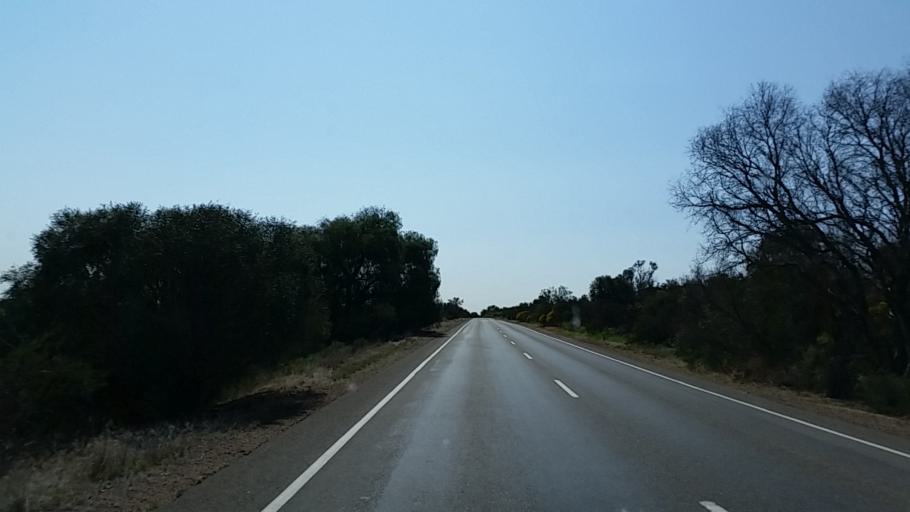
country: AU
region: South Australia
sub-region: Port Pirie City and Dists
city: Crystal Brook
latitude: -33.2371
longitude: 138.3871
